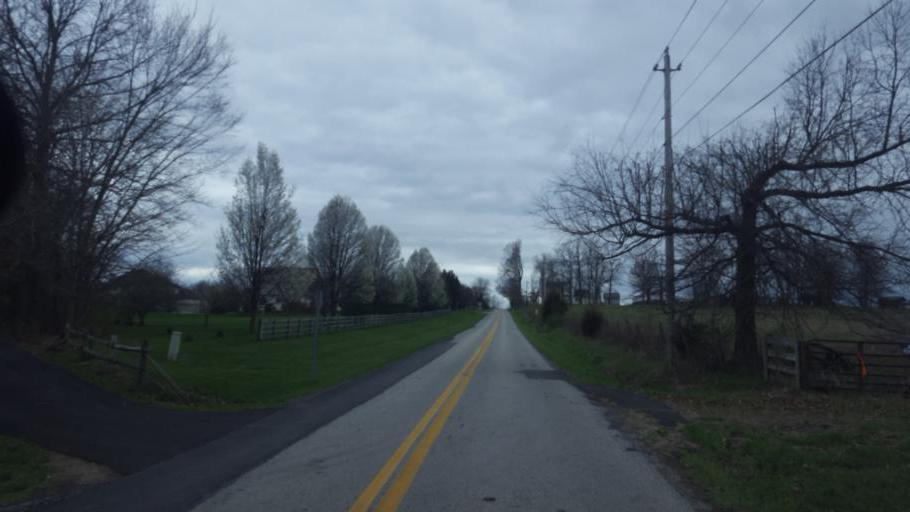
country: US
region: Ohio
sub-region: Delaware County
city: Sunbury
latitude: 40.2079
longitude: -82.8985
